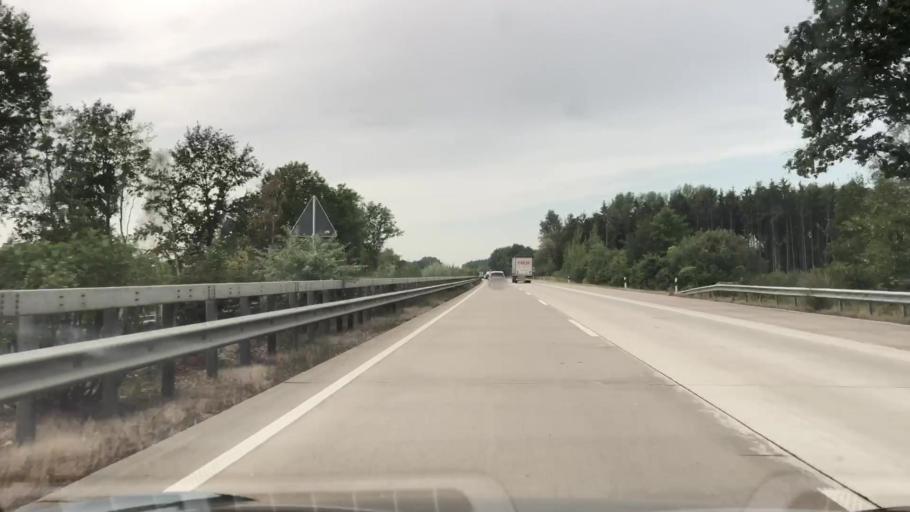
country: DE
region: Lower Saxony
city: Prinzhofte
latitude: 52.9398
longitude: 8.5130
